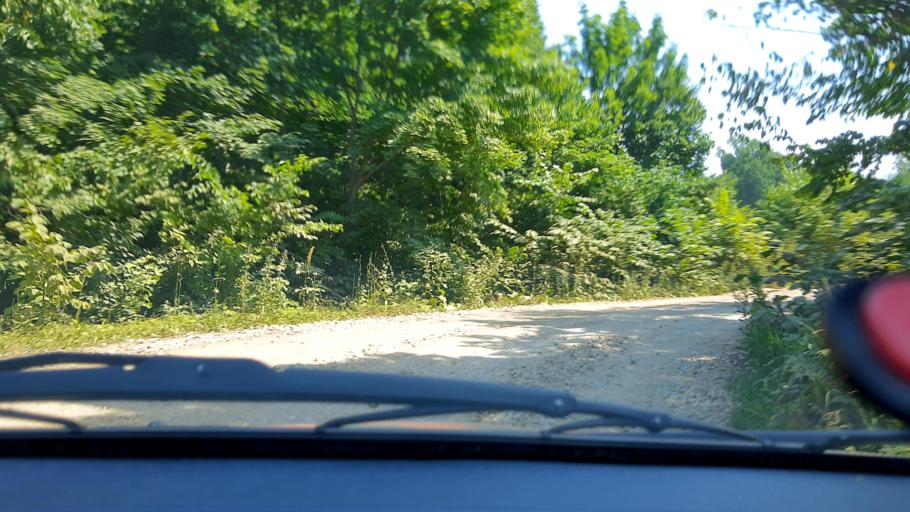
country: RU
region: Bashkortostan
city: Karmaskaly
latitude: 54.3900
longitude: 55.9009
